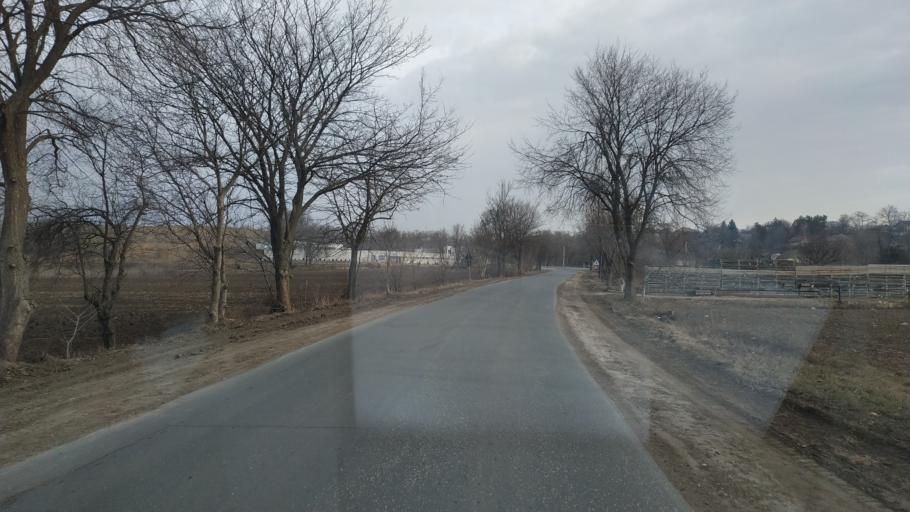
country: MD
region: Chisinau
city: Singera
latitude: 46.9249
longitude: 29.0475
